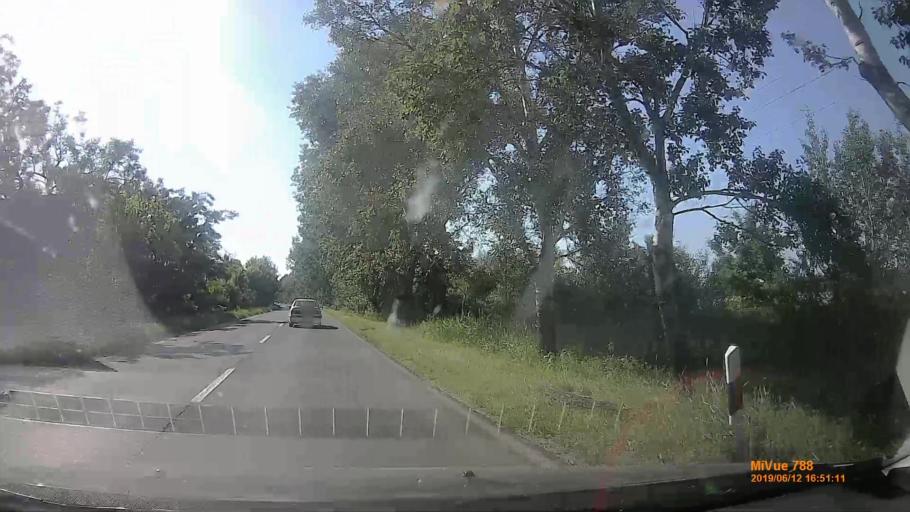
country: HU
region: Csongrad
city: Kiszombor
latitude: 46.2056
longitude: 20.3814
